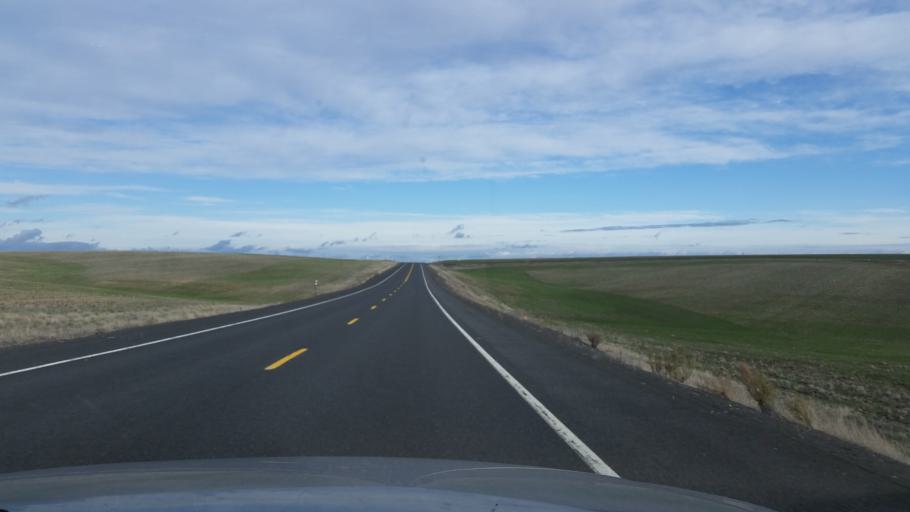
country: US
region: Washington
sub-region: Adams County
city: Ritzville
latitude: 47.3939
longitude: -118.4054
